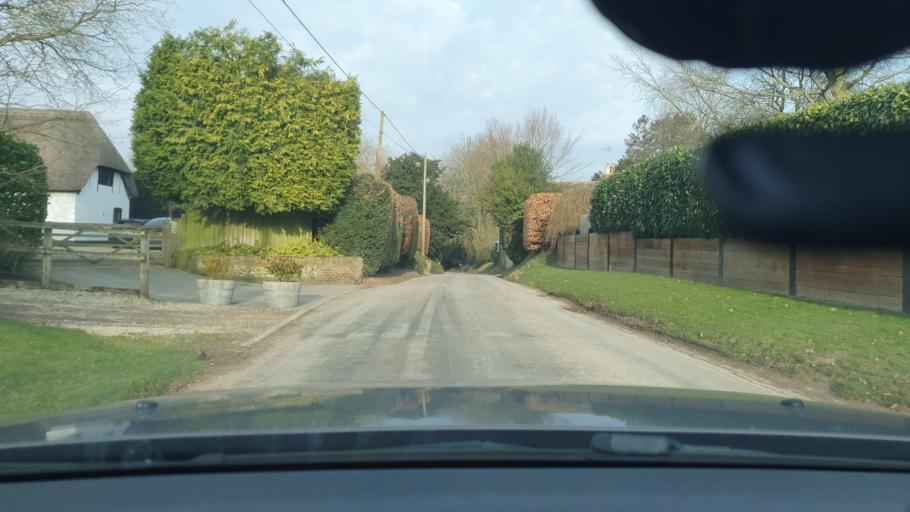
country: GB
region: England
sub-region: Wiltshire
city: Shalbourne
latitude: 51.3611
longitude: -1.5475
